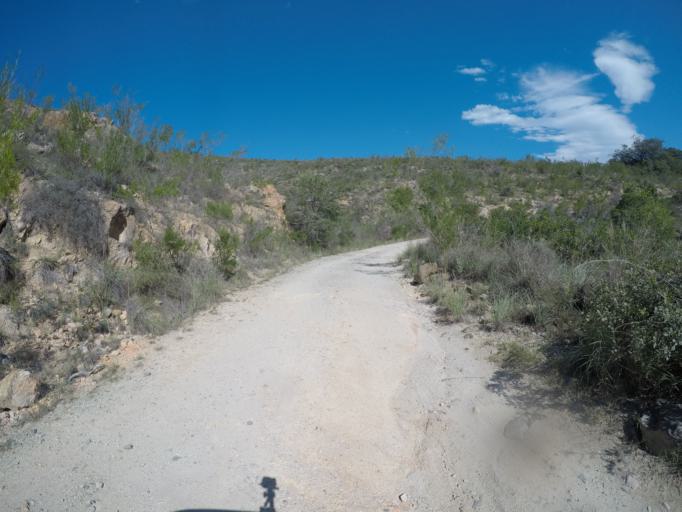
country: ZA
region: Eastern Cape
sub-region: Cacadu District Municipality
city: Kareedouw
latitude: -33.6466
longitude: 24.4625
